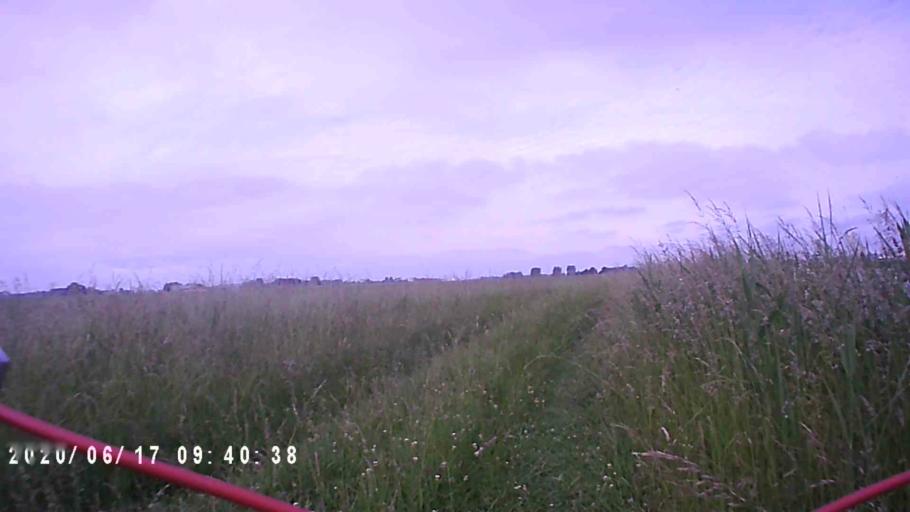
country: NL
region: Groningen
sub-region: Gemeente De Marne
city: Ulrum
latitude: 53.3516
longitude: 6.3615
